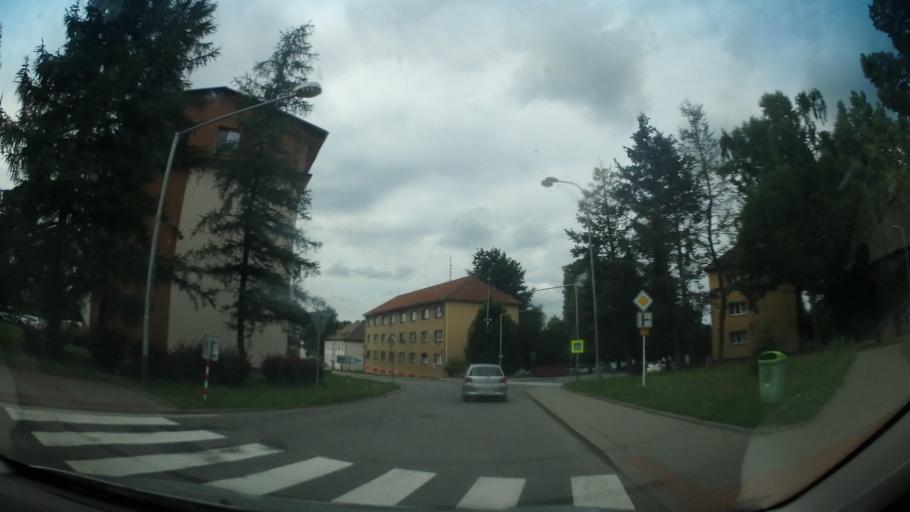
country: CZ
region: Vysocina
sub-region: Okres Zd'ar nad Sazavou
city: Nove Mesto na Morave
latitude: 49.5683
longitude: 16.0794
